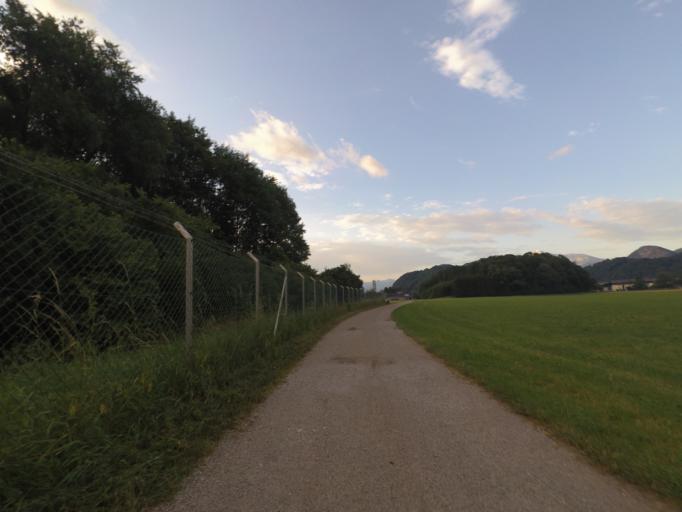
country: AT
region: Salzburg
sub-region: Politischer Bezirk Salzburg-Umgebung
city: Grodig
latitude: 47.7335
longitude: 13.0411
